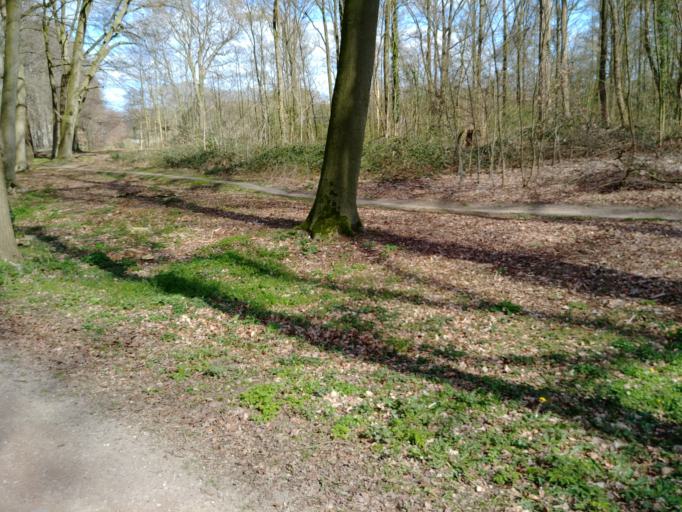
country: NL
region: Overijssel
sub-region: Gemeente Olst-Wijhe
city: Boskamp
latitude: 52.2911
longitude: 6.1294
